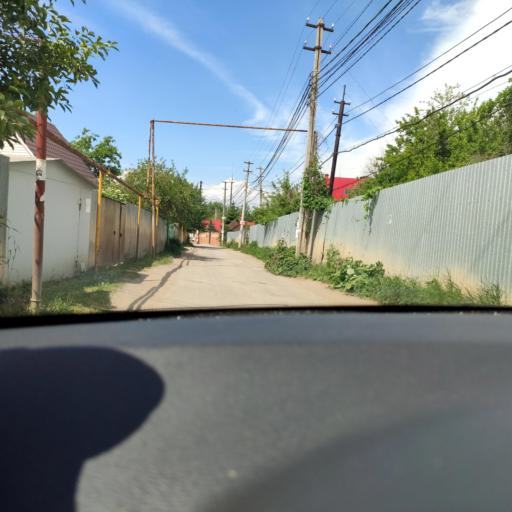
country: RU
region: Samara
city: Novokuybyshevsk
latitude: 53.1479
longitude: 50.0143
